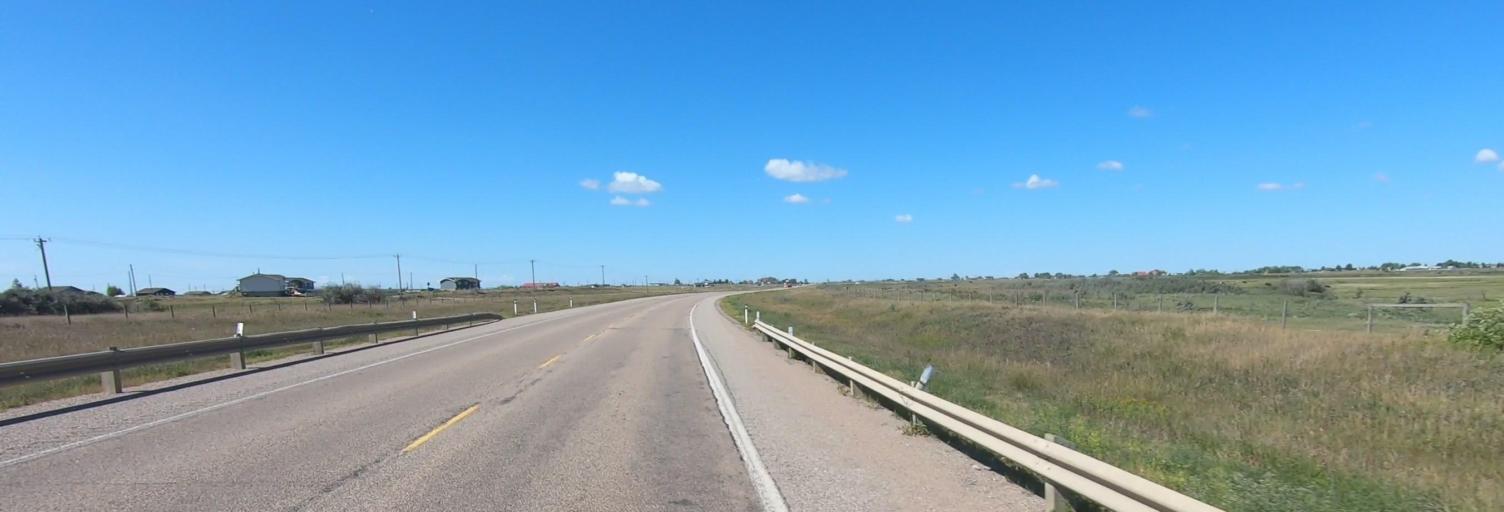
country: CA
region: Alberta
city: Strathmore
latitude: 50.8496
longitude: -113.0308
